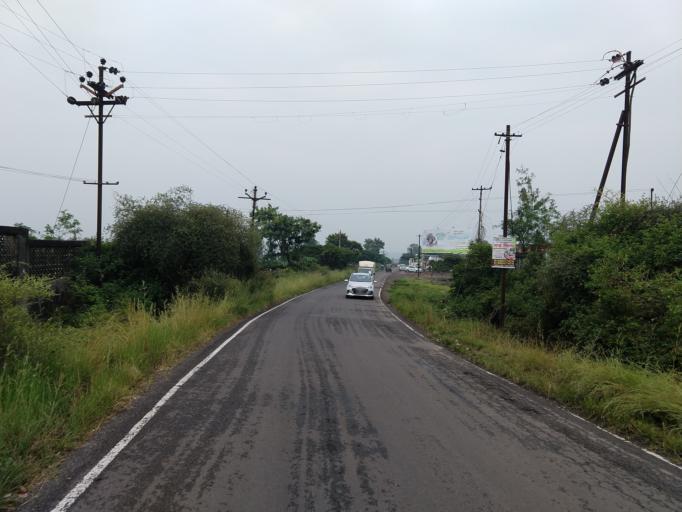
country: IN
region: Maharashtra
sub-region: Pune Division
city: Khed
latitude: 18.4035
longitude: 73.9114
